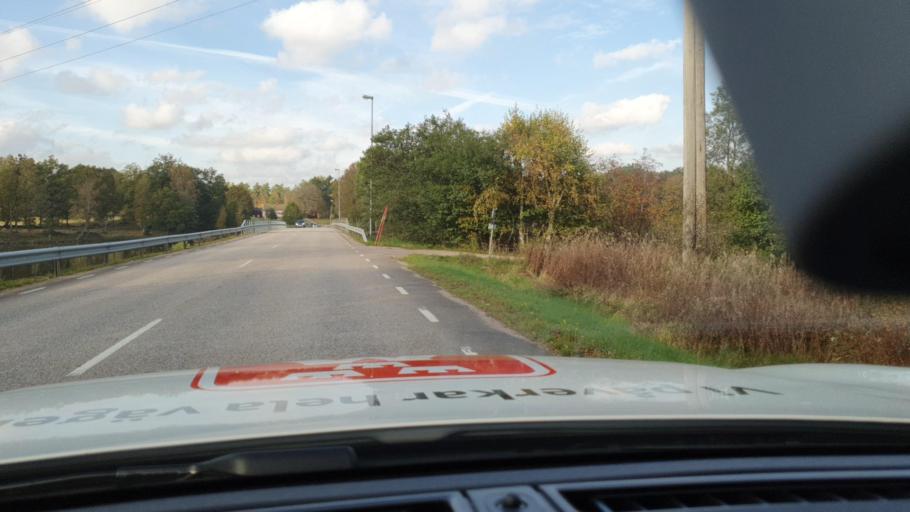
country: SE
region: Kronoberg
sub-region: Markaryds Kommun
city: Markaryd
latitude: 56.4887
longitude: 13.5280
